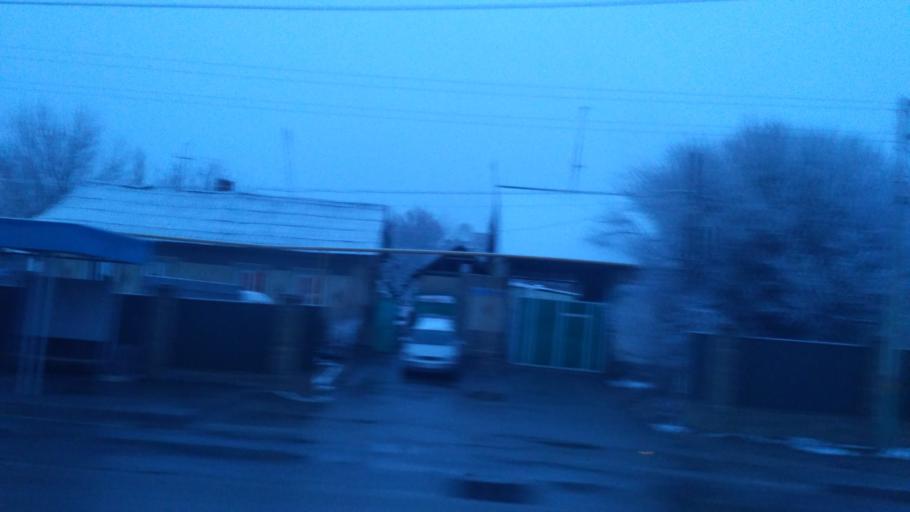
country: KZ
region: Ongtustik Qazaqstan
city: Shymkent
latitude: 42.3715
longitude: 69.5055
